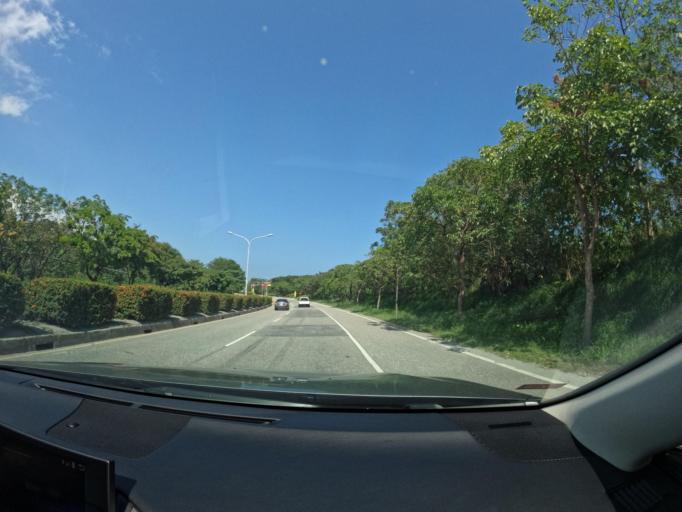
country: TW
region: Taiwan
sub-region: Hualien
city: Hualian
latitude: 23.9240
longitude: 121.5896
